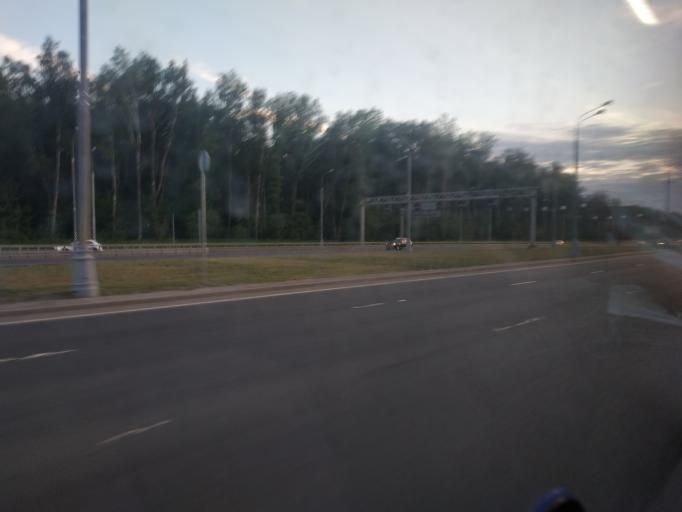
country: RU
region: Moscow
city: Solntsevo
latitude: 55.6097
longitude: 37.3910
